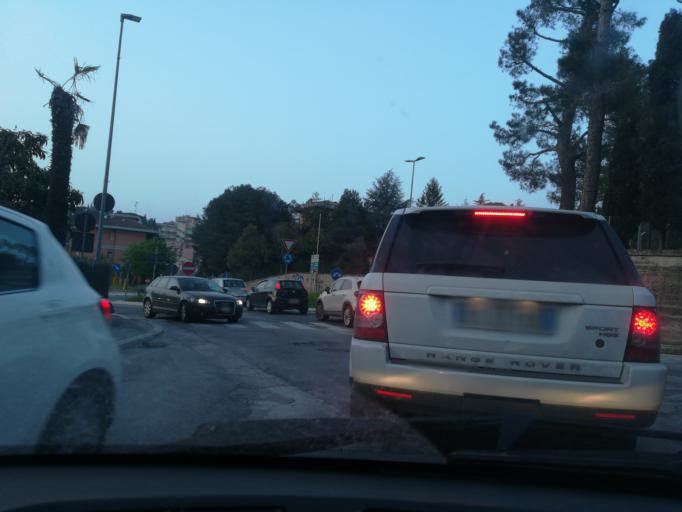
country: IT
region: The Marches
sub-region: Provincia di Macerata
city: Macerata
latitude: 43.2902
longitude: 13.4564
